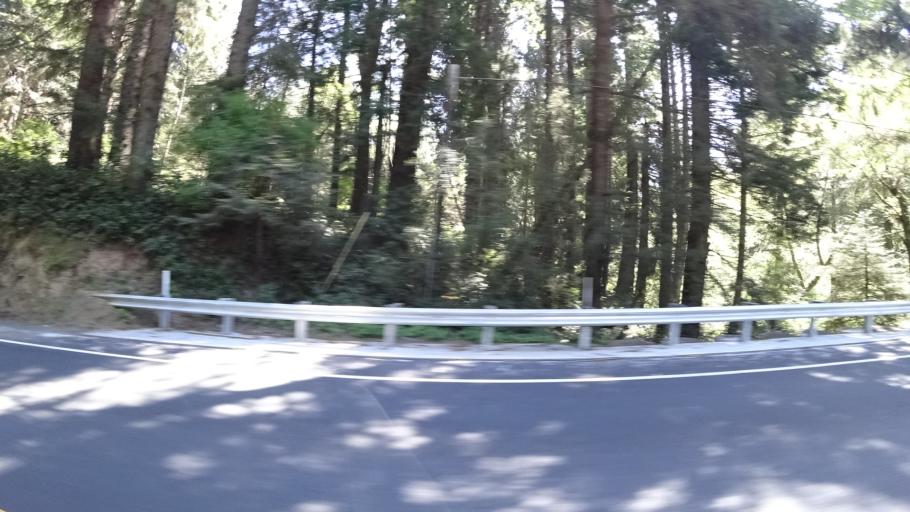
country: US
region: California
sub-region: Humboldt County
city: Westhaven-Moonstone
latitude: 41.1693
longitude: -124.1020
